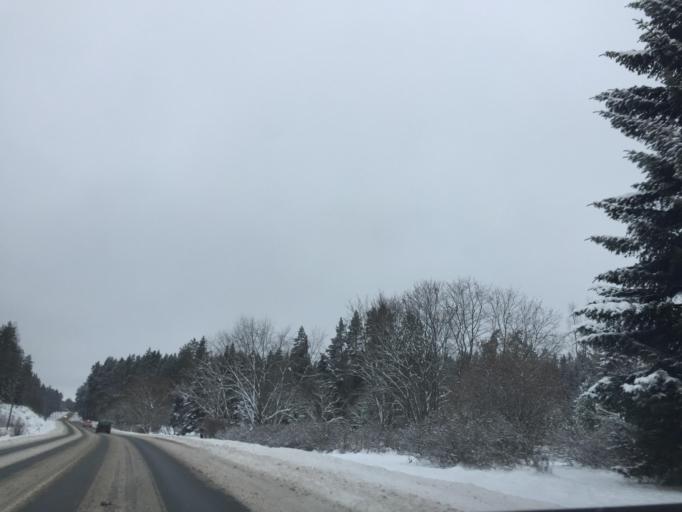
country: LV
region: Smiltene
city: Smiltene
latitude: 57.4028
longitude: 25.9538
